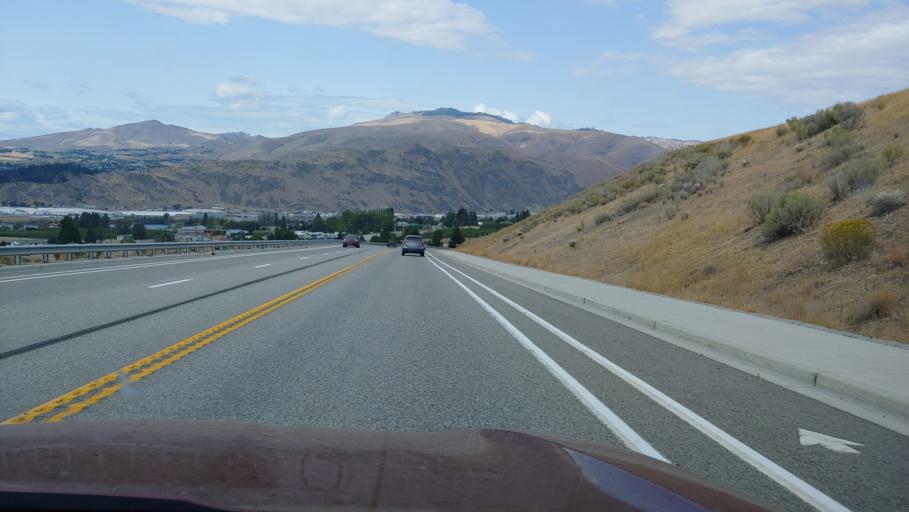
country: US
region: Washington
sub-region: Douglas County
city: East Wenatchee Bench
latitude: 47.4635
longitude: -120.2943
